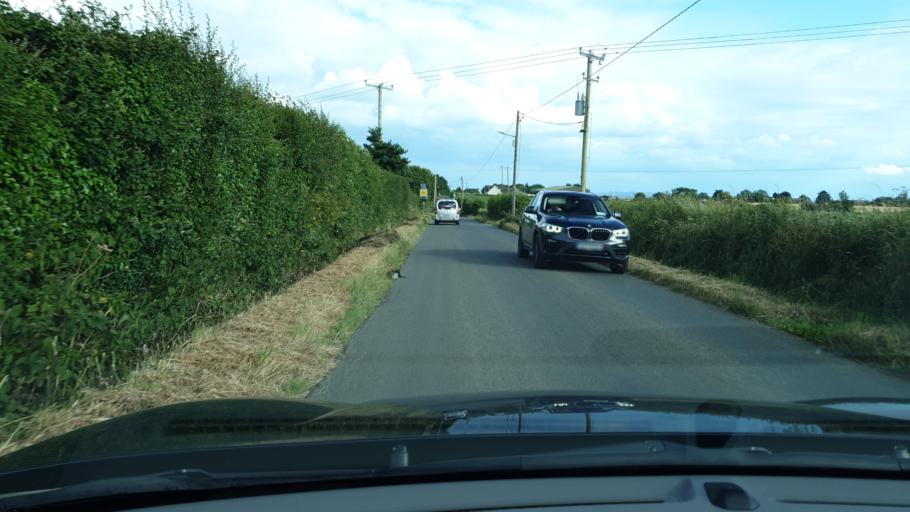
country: IE
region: Leinster
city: Lusk
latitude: 53.5660
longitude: -6.1491
